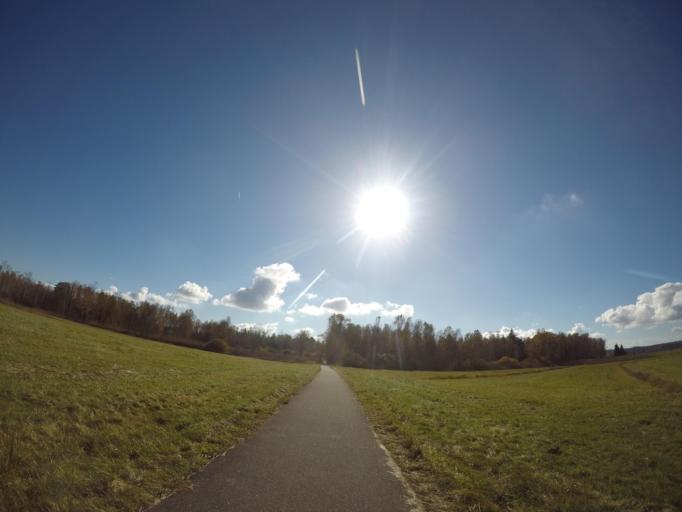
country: DE
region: Baden-Wuerttemberg
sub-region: Tuebingen Region
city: Bad Buchau
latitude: 48.0833
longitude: 9.5982
